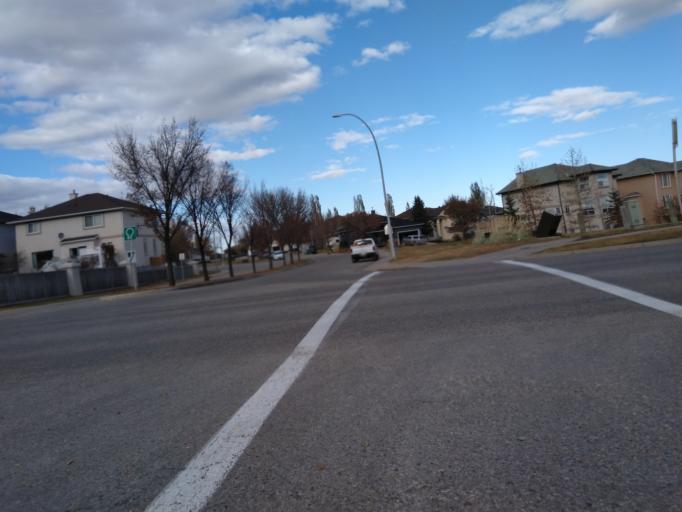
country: CA
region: Alberta
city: Calgary
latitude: 51.1388
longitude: -114.1297
